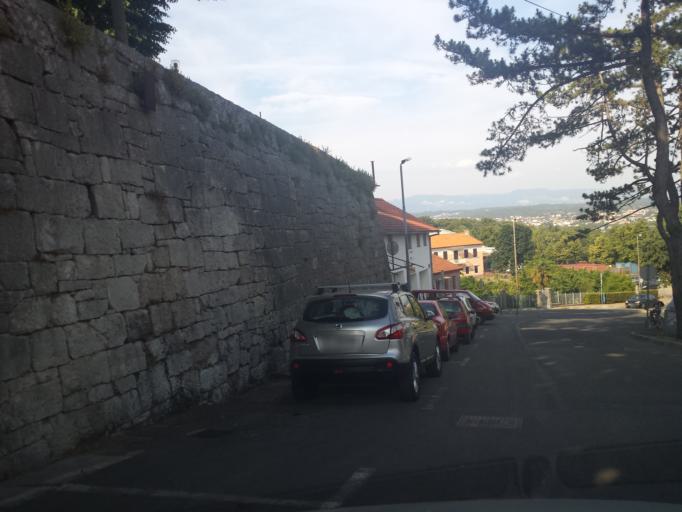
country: HR
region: Primorsko-Goranska
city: Kastav
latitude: 45.3717
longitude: 14.3502
